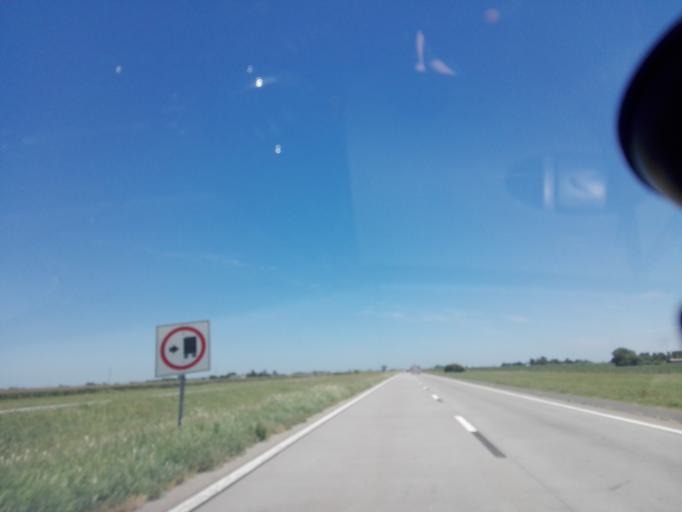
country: AR
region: Santa Fe
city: Armstrong
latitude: -32.8156
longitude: -61.5702
